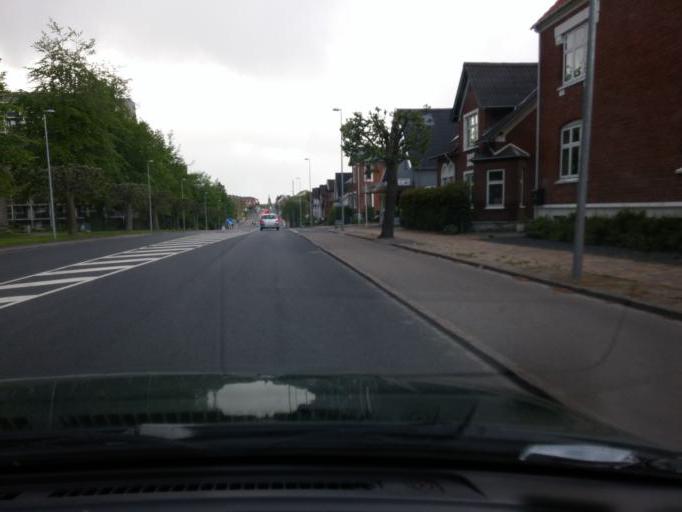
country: DK
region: South Denmark
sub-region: Odense Kommune
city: Odense
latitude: 55.3932
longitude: 10.4193
